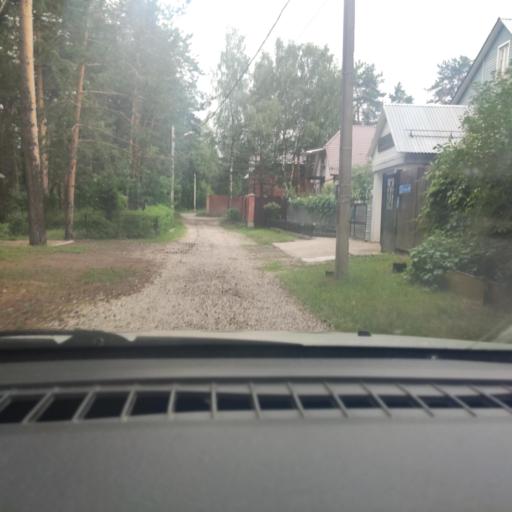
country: RU
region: Perm
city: Perm
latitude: 58.0628
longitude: 56.3087
